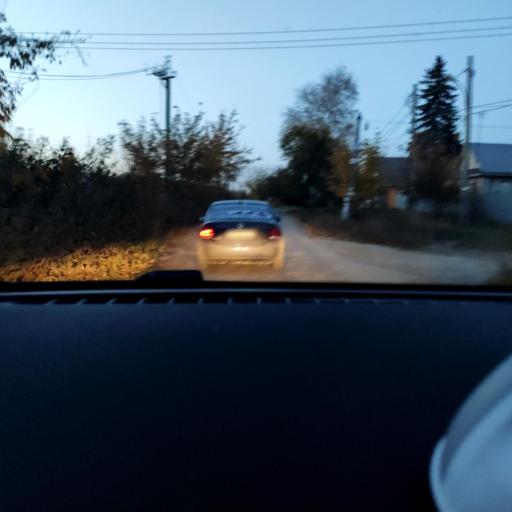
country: RU
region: Samara
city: Petra-Dubrava
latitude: 53.2976
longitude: 50.3040
